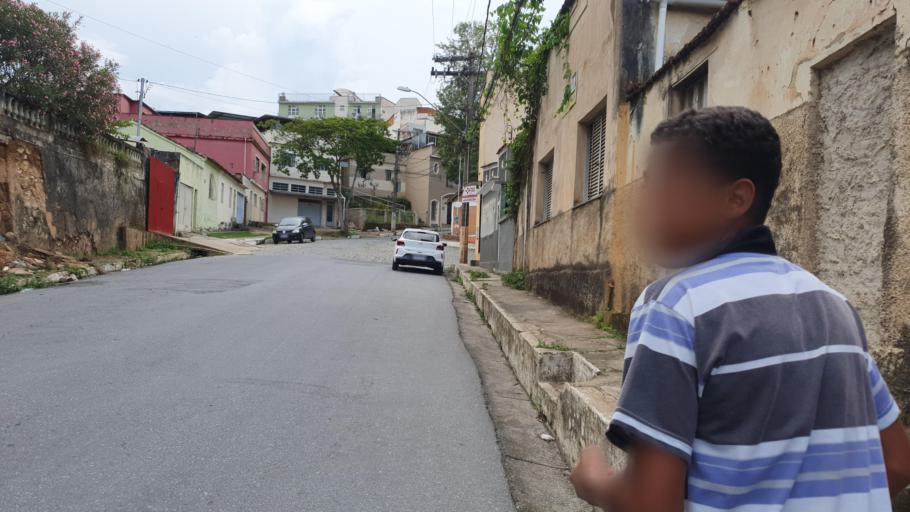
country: BR
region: Minas Gerais
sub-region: Sao Joao Del Rei
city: Sao Joao del Rei
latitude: -21.1288
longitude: -44.2641
